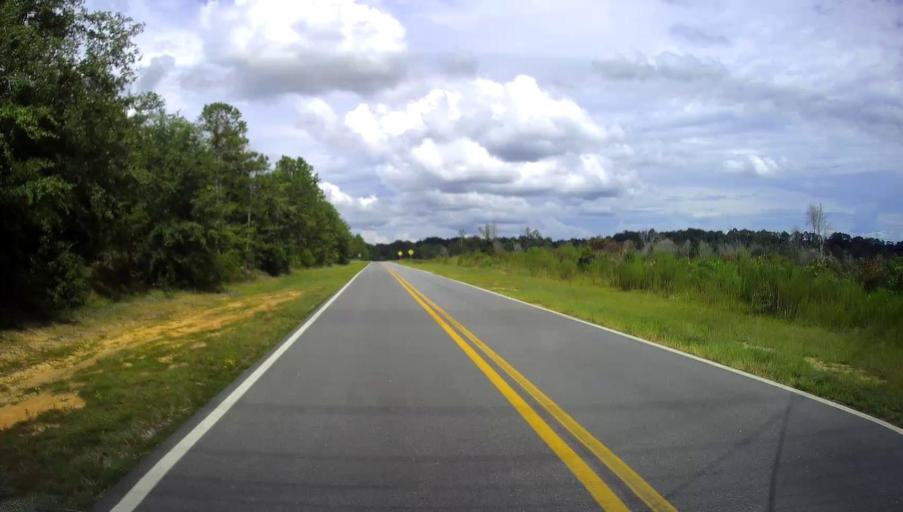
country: US
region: Georgia
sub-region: Chattahoochee County
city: Cusseta
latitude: 32.3071
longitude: -84.7629
